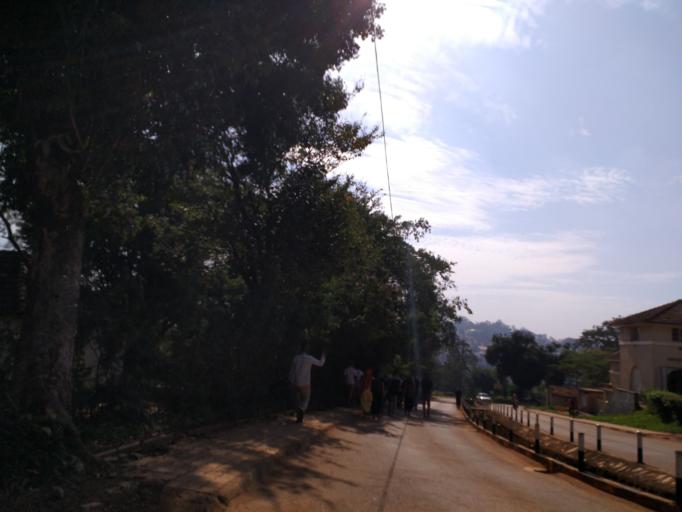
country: UG
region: Central Region
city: Kampala Central Division
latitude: 0.3369
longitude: 32.5687
